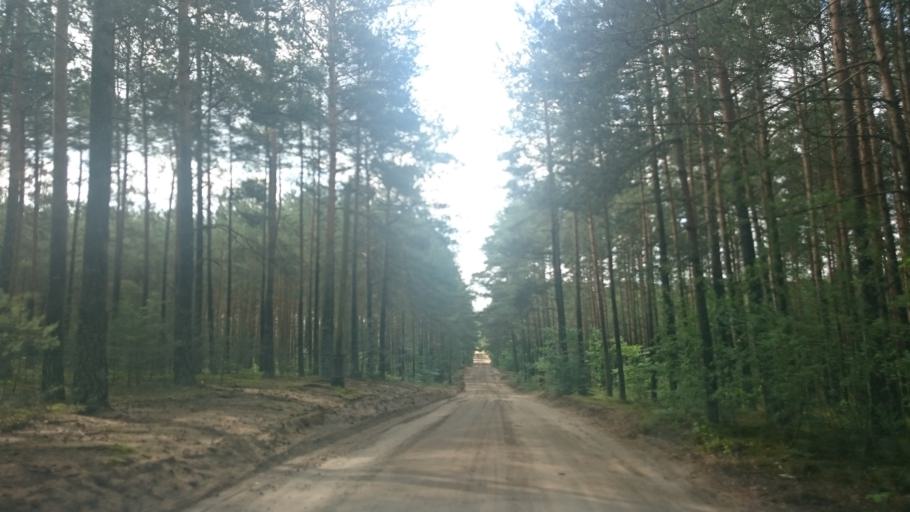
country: PL
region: Pomeranian Voivodeship
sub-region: Powiat koscierski
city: Karsin
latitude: 53.9854
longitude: 17.9311
